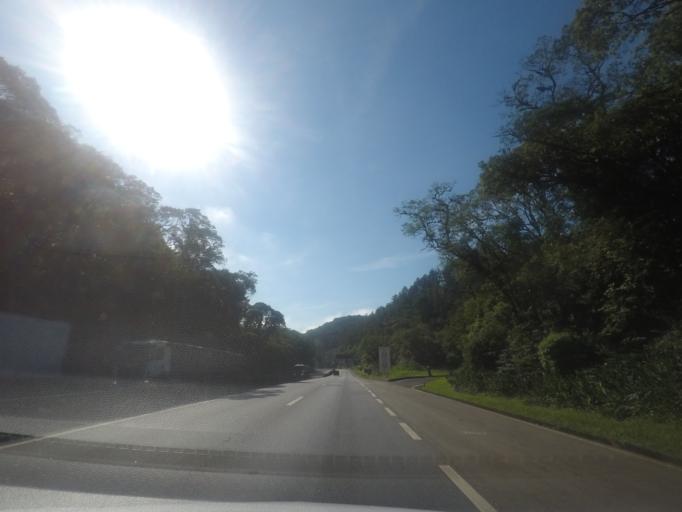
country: BR
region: Parana
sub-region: Piraquara
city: Piraquara
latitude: -25.5969
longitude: -48.9022
